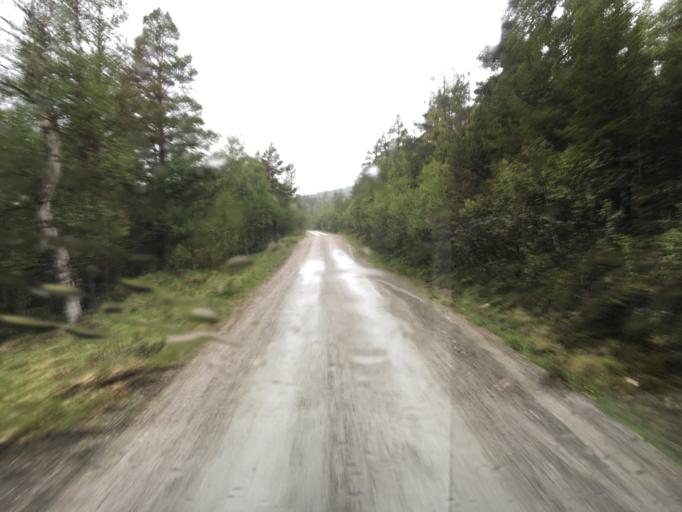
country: NO
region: Hedmark
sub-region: Folldal
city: Folldal
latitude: 62.0663
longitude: 9.9224
